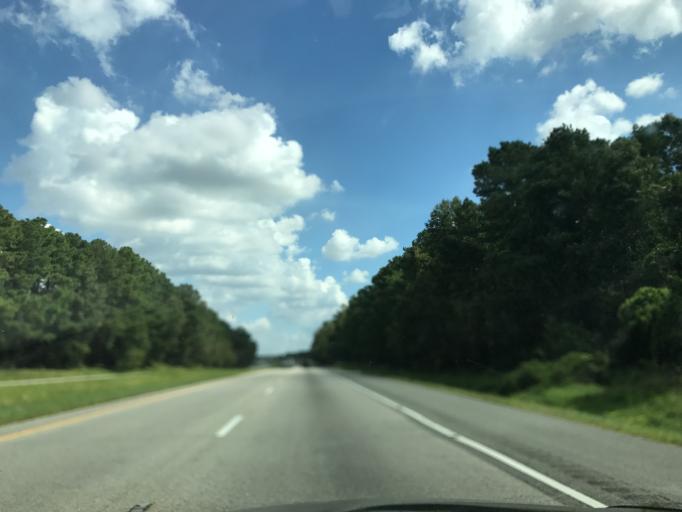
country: US
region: Maryland
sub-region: Queen Anne's County
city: Grasonville
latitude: 38.9925
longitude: -76.1381
